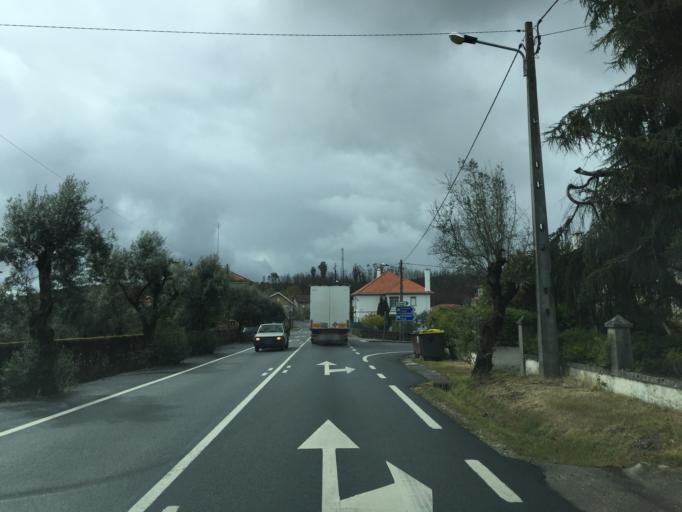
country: PT
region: Coimbra
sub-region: Oliveira do Hospital
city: Oliveira do Hospital
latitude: 40.3241
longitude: -7.9203
